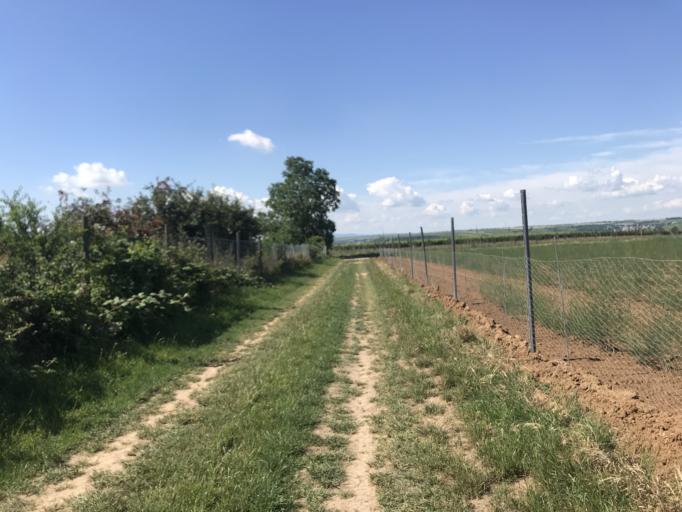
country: DE
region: Rheinland-Pfalz
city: Stadecken-Elsheim
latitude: 49.9295
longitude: 8.1160
